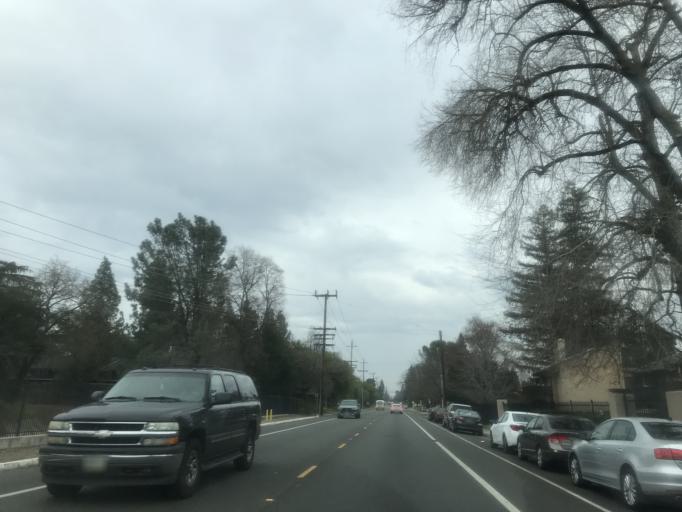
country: US
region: California
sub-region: Sacramento County
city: Arden-Arcade
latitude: 38.5816
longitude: -121.4094
